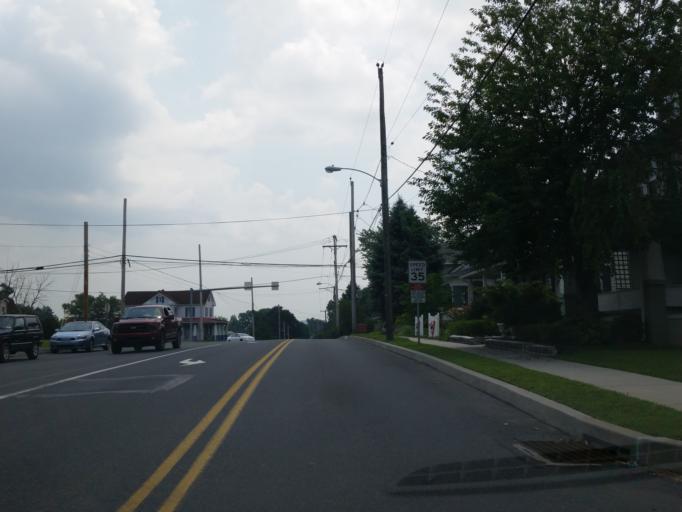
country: US
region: Pennsylvania
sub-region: Dauphin County
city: Palmdale
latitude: 40.3006
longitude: -76.6095
